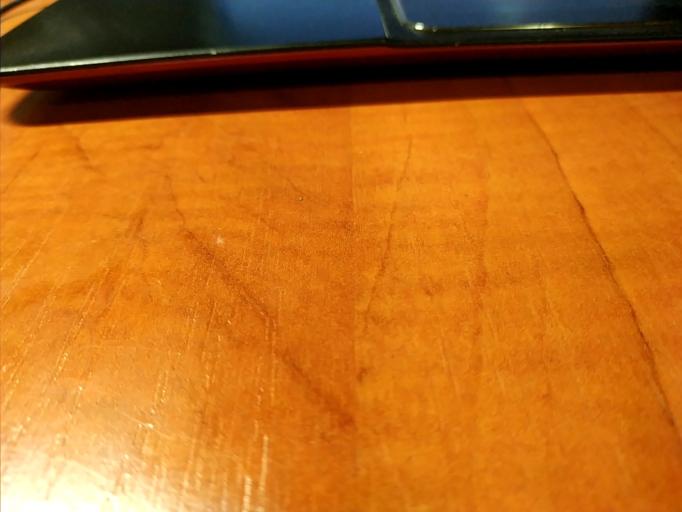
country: RU
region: Tverskaya
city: Ves'yegonsk
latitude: 58.8131
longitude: 37.5435
